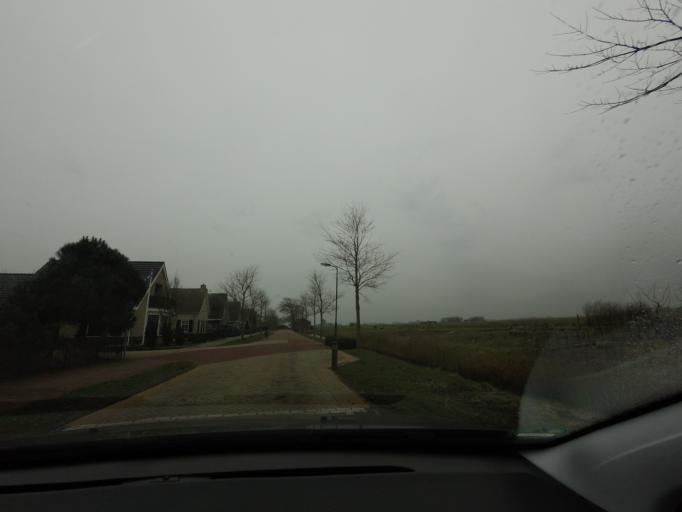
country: NL
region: Friesland
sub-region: Gemeente Franekeradeel
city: Tzum
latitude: 53.1617
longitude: 5.5616
